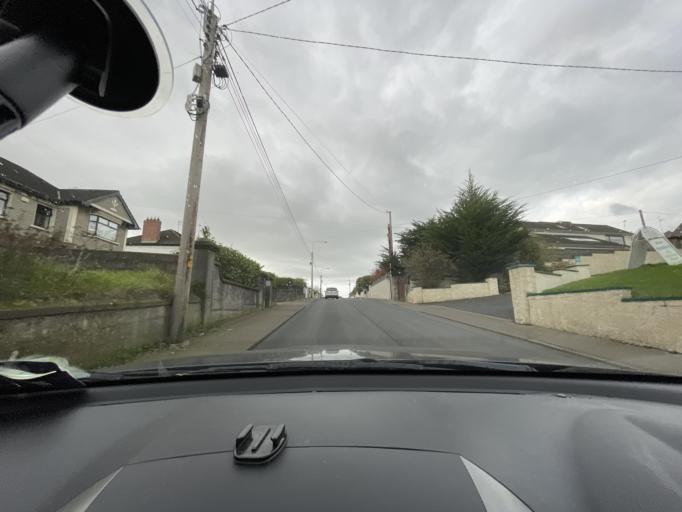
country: IE
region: Leinster
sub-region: Lu
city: Drogheda
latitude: 53.7194
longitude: -6.3341
